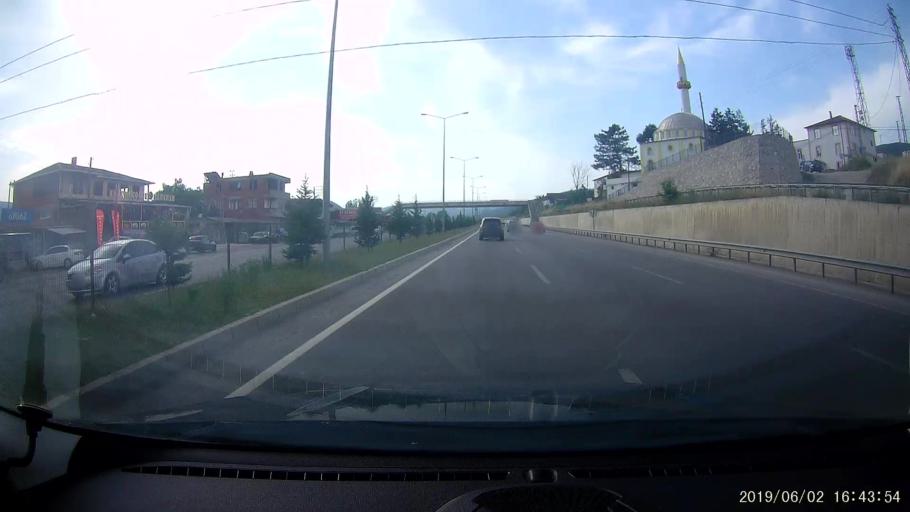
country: TR
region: Samsun
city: Kavak
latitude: 41.1424
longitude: 36.1188
